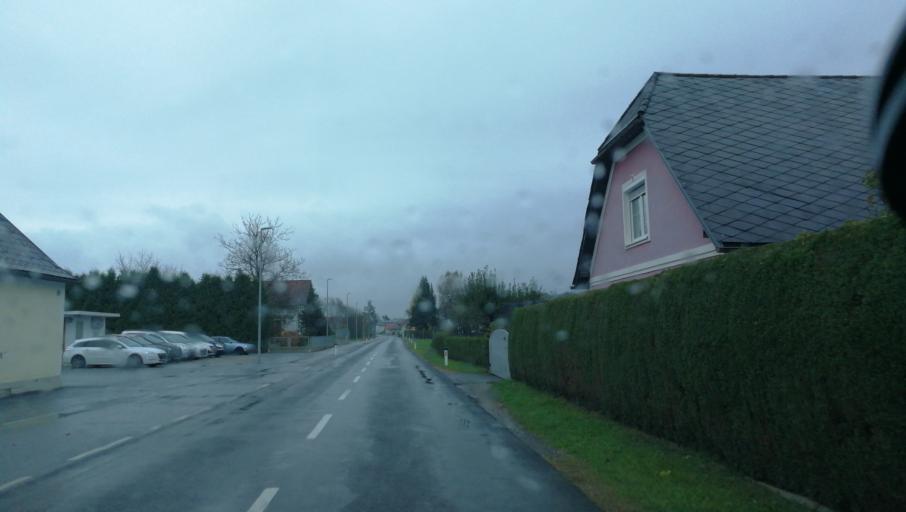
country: AT
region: Styria
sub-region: Politischer Bezirk Leibnitz
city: Spielfeld
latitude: 46.7128
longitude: 15.6389
